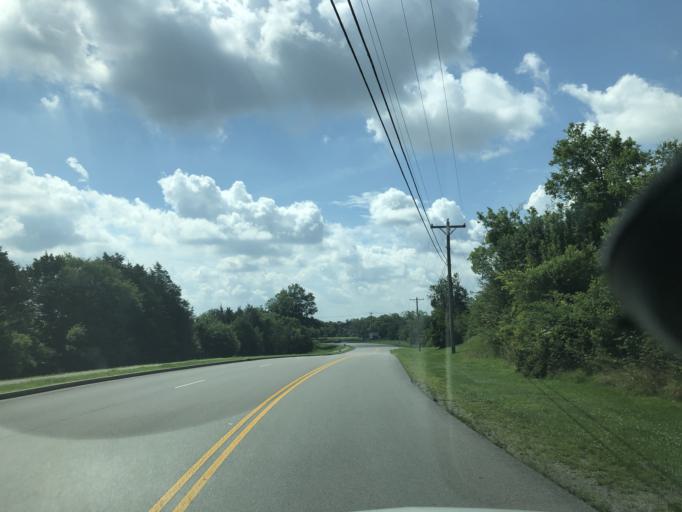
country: US
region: Tennessee
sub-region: Rutherford County
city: La Vergne
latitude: 36.0283
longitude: -86.6178
